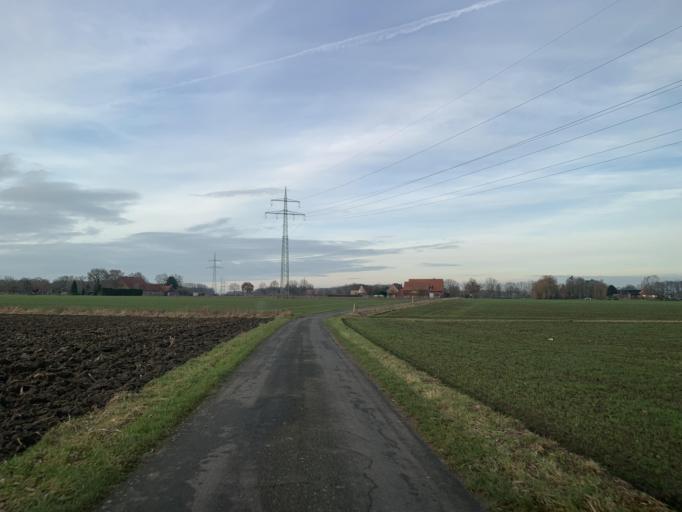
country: DE
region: North Rhine-Westphalia
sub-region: Regierungsbezirk Munster
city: Dulmen
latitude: 51.8334
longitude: 7.3302
